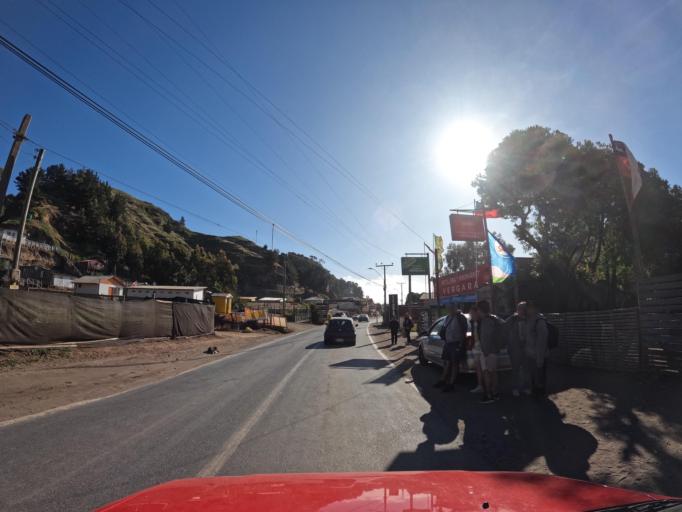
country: CL
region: Maule
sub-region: Provincia de Talca
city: Constitucion
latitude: -34.8849
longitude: -72.1607
